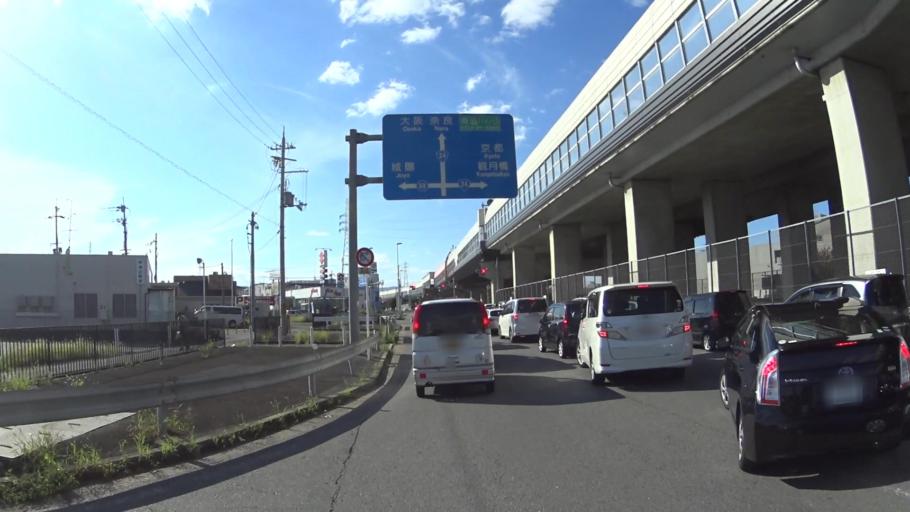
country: JP
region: Kyoto
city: Uji
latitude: 34.9038
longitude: 135.7863
